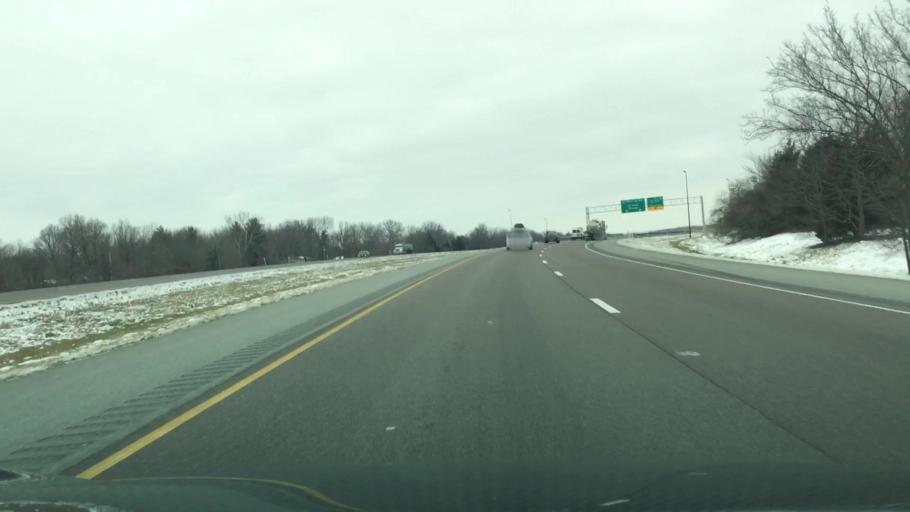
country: US
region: Illinois
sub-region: Jefferson County
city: Mount Vernon
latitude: 38.2644
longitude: -88.9306
